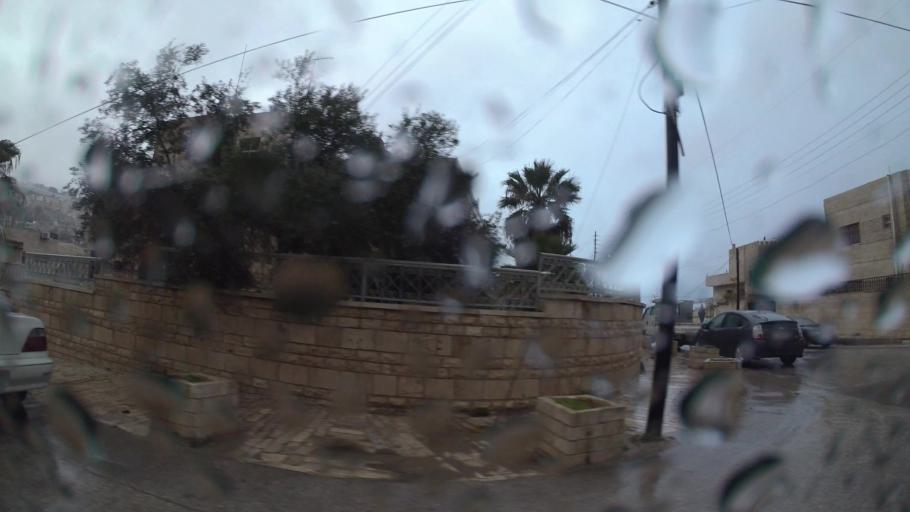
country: JO
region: Amman
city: Al Jubayhah
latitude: 32.0319
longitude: 35.8421
